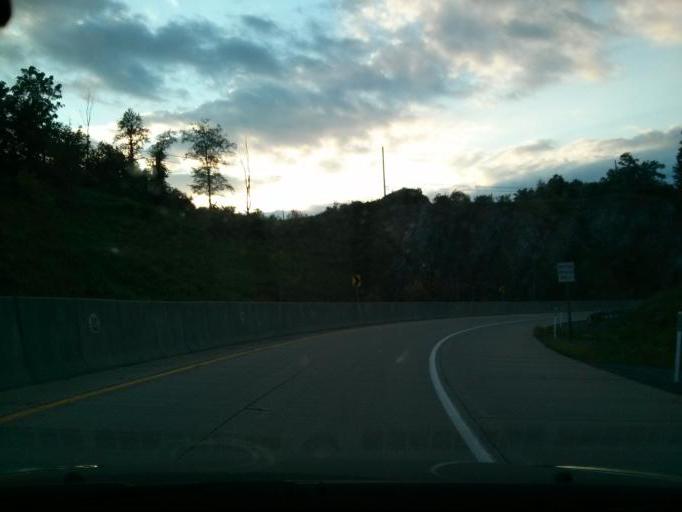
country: US
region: Pennsylvania
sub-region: Centre County
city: Park Forest Village
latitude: 40.8167
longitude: -77.9415
